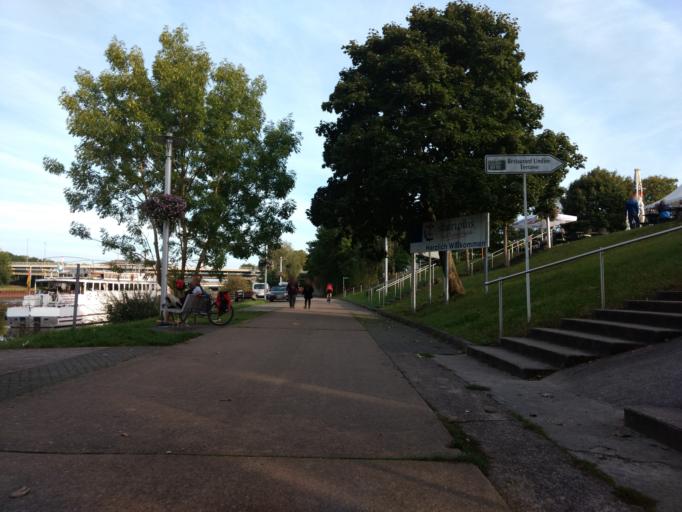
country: DE
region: Saarland
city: Saarlouis
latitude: 49.3236
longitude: 6.7444
